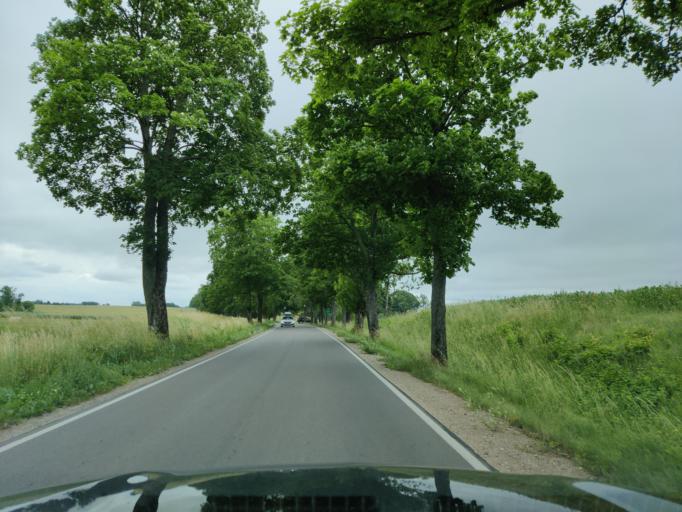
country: PL
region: Warmian-Masurian Voivodeship
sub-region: Powiat mragowski
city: Mikolajki
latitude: 53.8665
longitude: 21.5977
